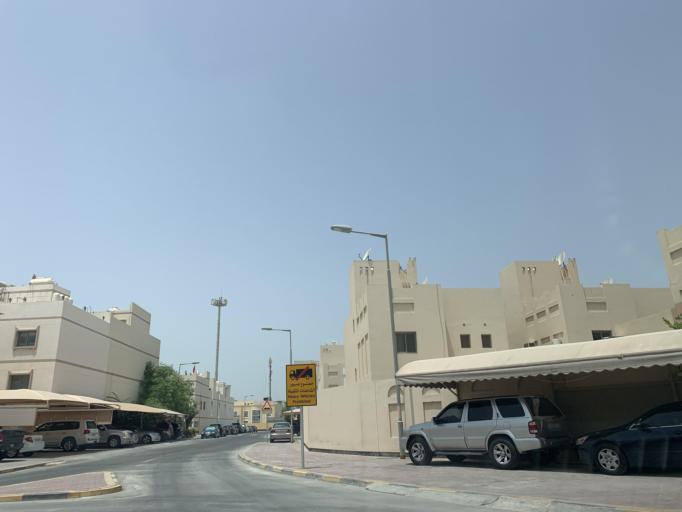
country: BH
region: Northern
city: Sitrah
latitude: 26.1466
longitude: 50.5887
